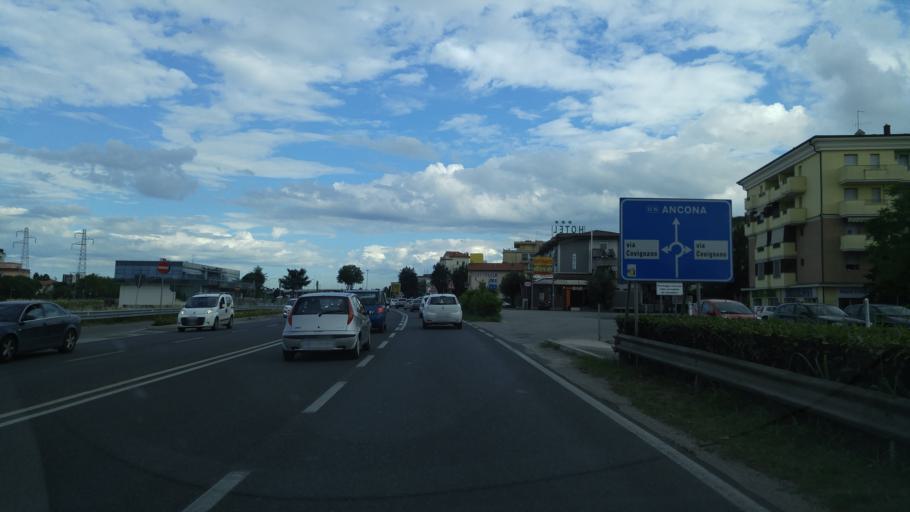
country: IT
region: Emilia-Romagna
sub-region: Provincia di Rimini
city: Rimini
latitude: 44.0479
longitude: 12.5504
